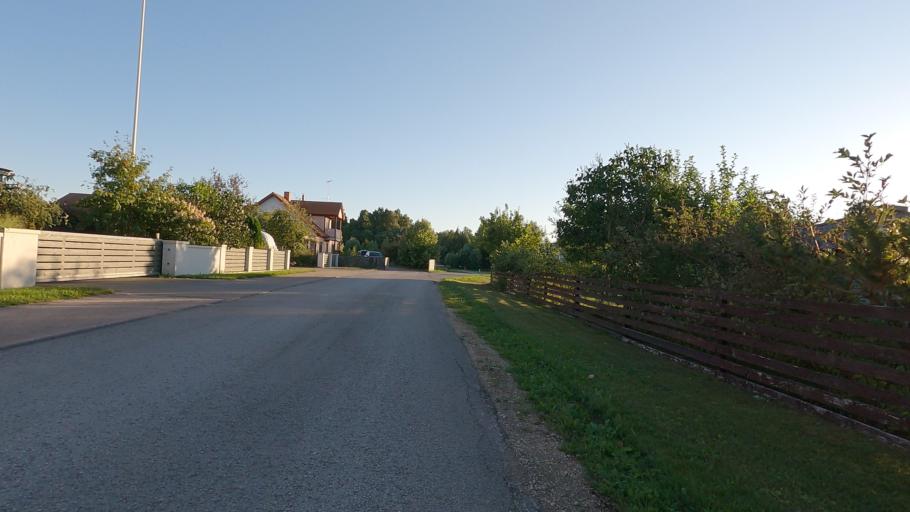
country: EE
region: Raplamaa
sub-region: Rapla vald
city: Rapla
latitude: 59.0042
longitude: 24.7787
